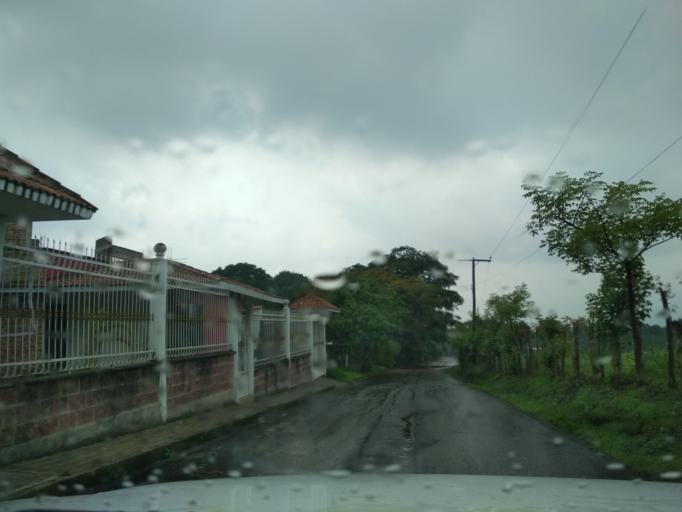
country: MX
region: Veracruz
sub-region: Ixhuatlancillo
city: San Isidro
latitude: 18.9033
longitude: -97.1211
